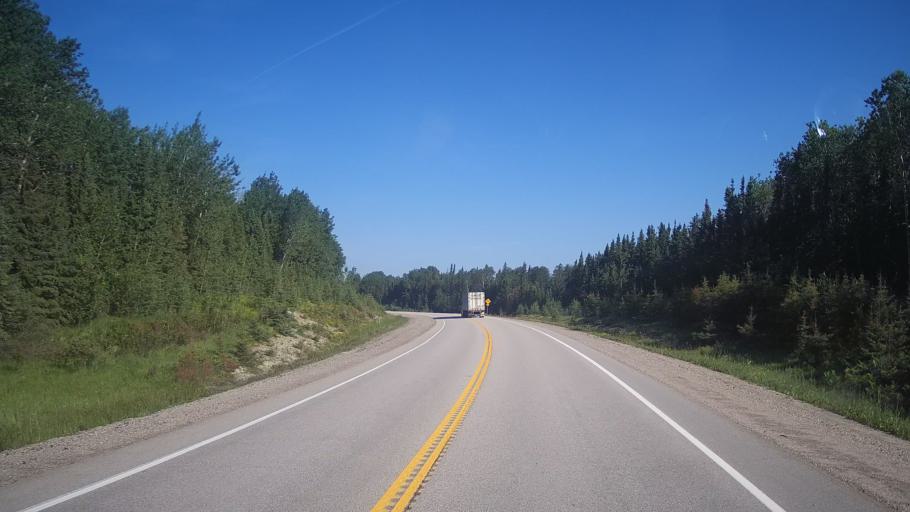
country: CA
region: Ontario
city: Dryden
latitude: 49.5844
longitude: -92.2642
